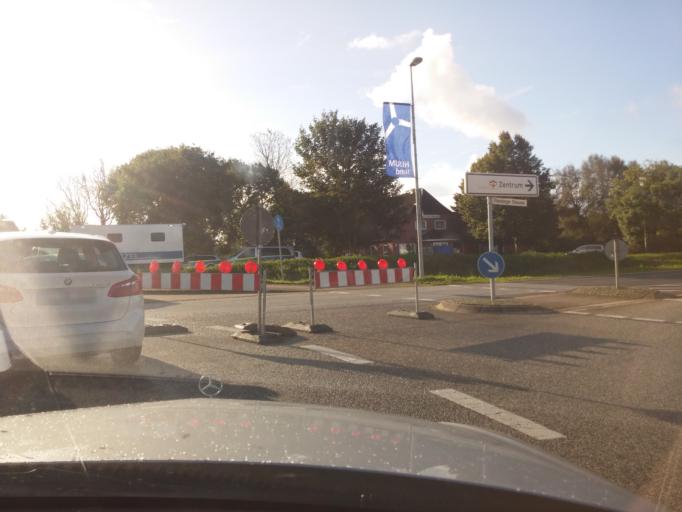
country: DE
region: Schleswig-Holstein
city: Mildstedt
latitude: 54.4934
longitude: 9.0856
